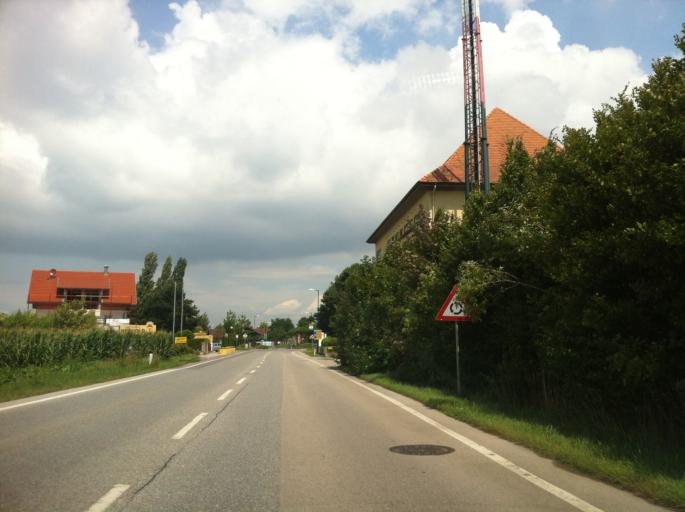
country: AT
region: Lower Austria
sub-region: Politischer Bezirk Tulln
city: Tulln
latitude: 48.3171
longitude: 16.0569
